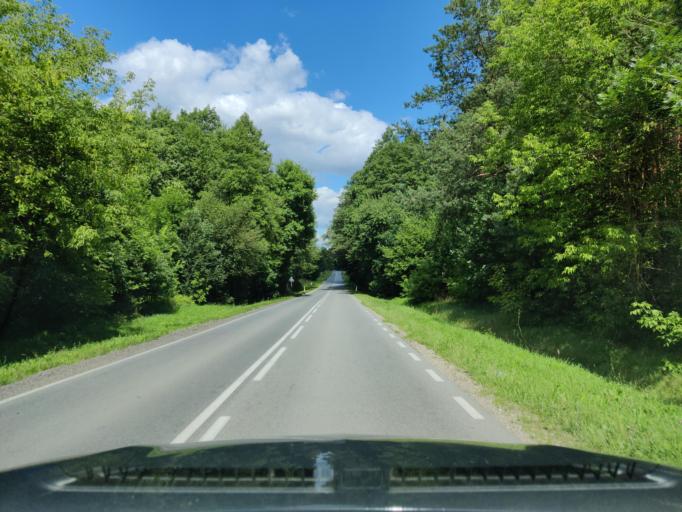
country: PL
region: Masovian Voivodeship
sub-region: Powiat wegrowski
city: Grebkow
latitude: 52.2246
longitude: 21.8780
